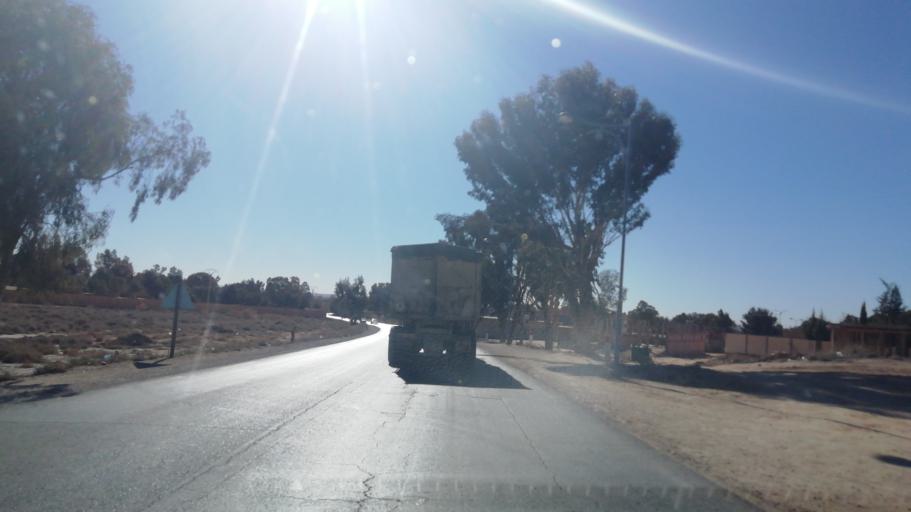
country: DZ
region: Saida
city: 'Ain el Hadjar
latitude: 34.1485
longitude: 0.0698
